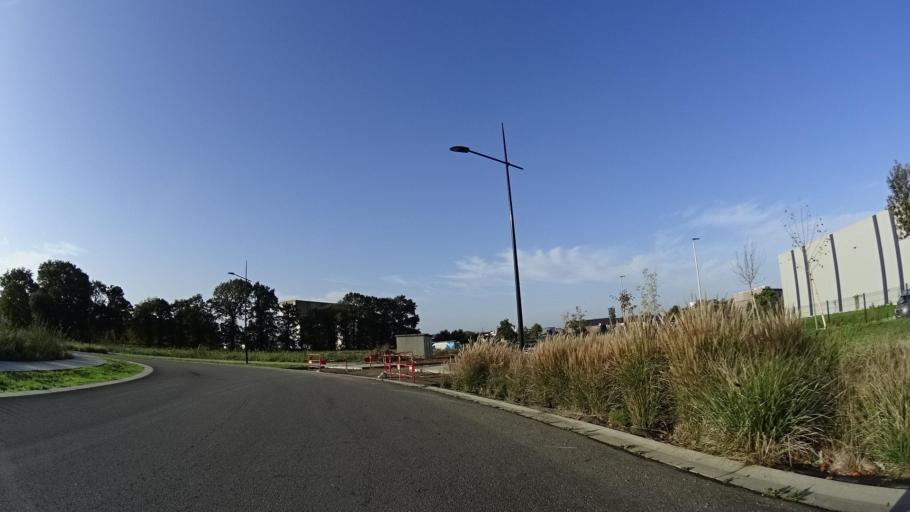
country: FR
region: Brittany
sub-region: Departement d'Ille-et-Vilaine
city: Pace
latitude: 48.1426
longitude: -1.7635
